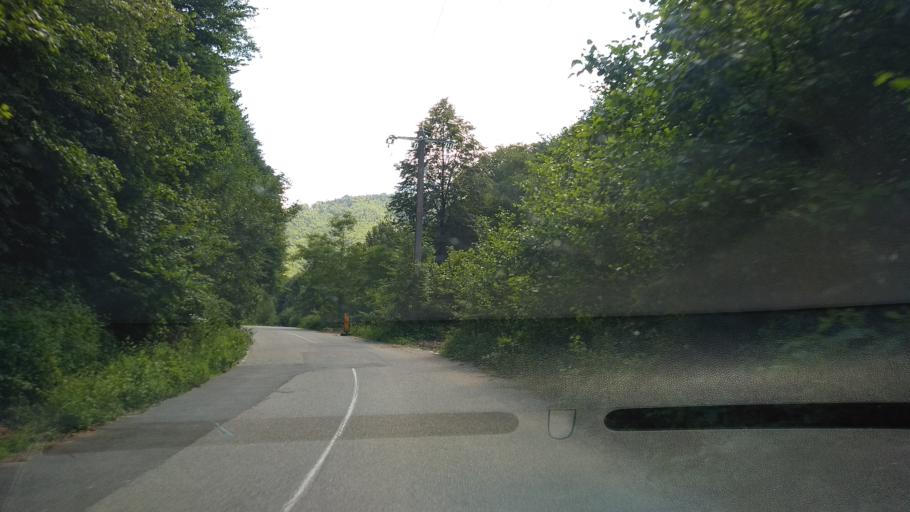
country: RO
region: Hunedoara
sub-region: Comuna Orastioara de Sus
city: Orastioara de Sus
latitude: 45.6670
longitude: 23.1706
